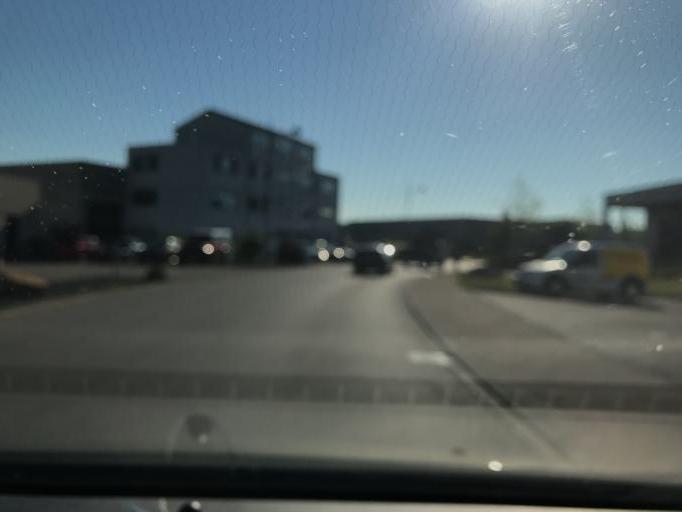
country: LU
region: Luxembourg
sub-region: Canton de Luxembourg
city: Niederanven
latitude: 49.6445
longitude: 6.2682
